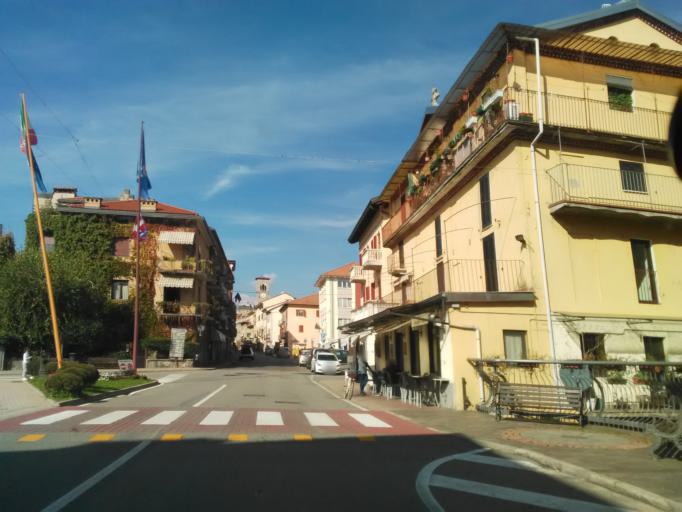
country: IT
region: Piedmont
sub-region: Provincia di Vercelli
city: Serravalle Sesia
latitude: 45.6854
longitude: 8.3123
